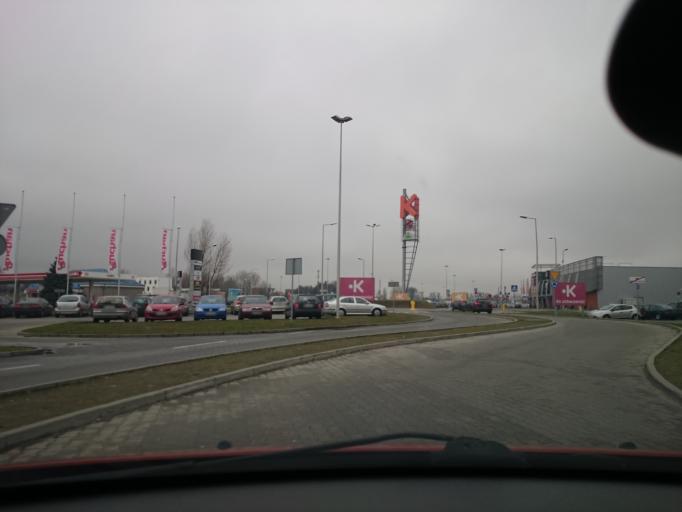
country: PL
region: Opole Voivodeship
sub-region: Powiat opolski
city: Chmielowice
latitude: 50.6807
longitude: 17.8813
